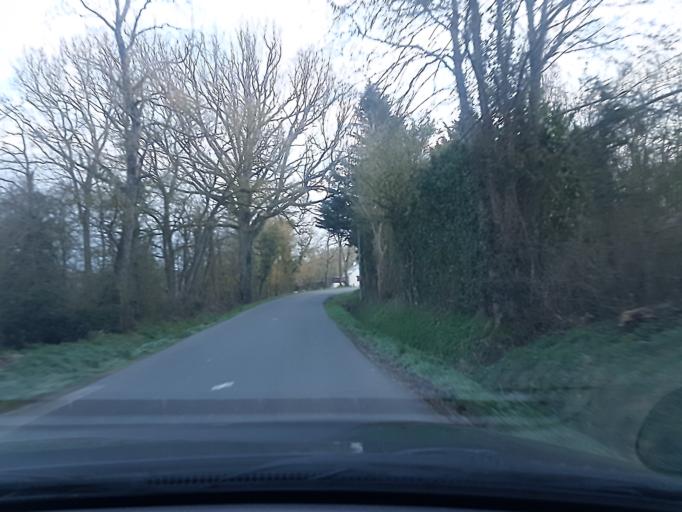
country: FR
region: Pays de la Loire
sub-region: Departement de la Loire-Atlantique
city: Saint-Mars-du-Desert
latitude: 47.3858
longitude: -1.4257
